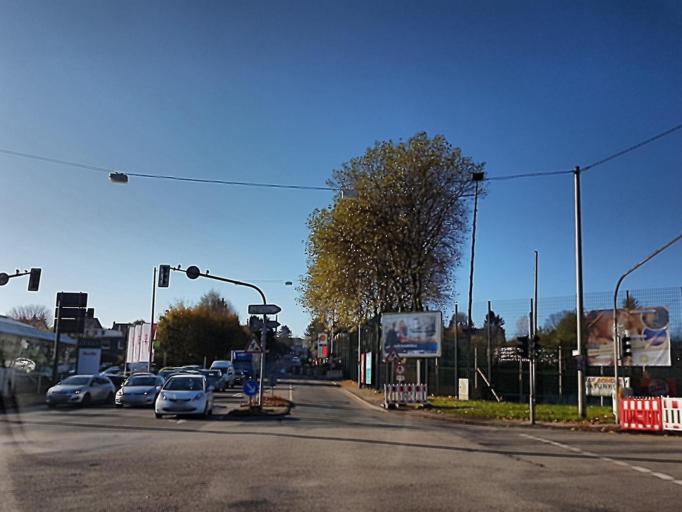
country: DE
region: North Rhine-Westphalia
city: Wermelskirchen
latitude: 51.1900
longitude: 7.2663
